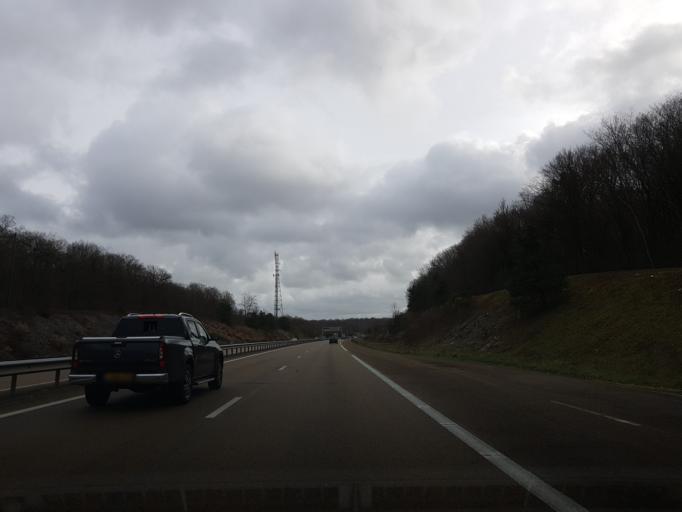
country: FR
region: Champagne-Ardenne
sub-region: Departement de la Haute-Marne
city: Chamarandes-Choignes
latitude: 48.0316
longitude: 5.0825
